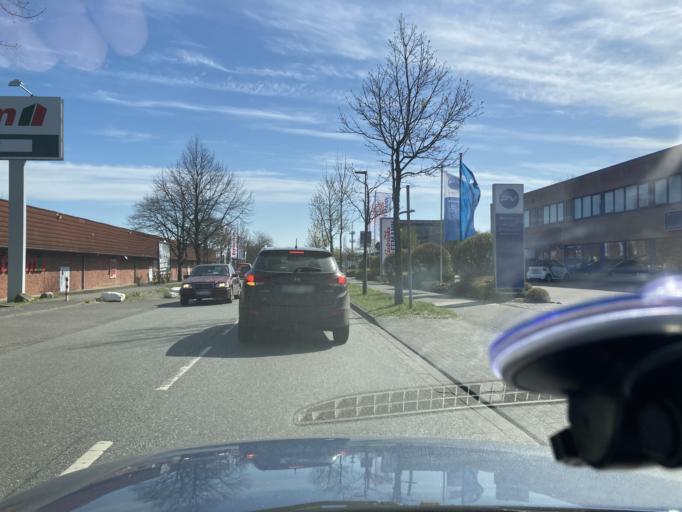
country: DE
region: Schleswig-Holstein
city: Heide
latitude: 54.1965
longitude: 9.1274
